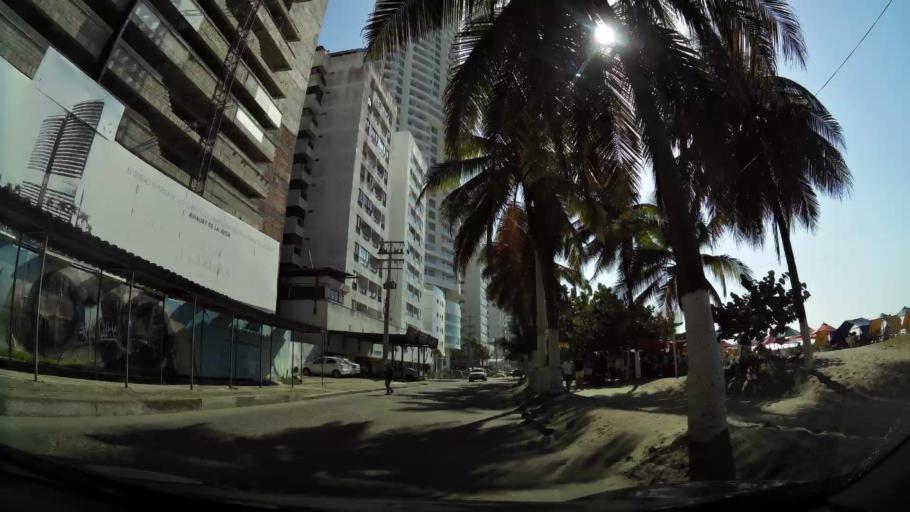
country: CO
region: Bolivar
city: Cartagena
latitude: 10.4037
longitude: -75.5561
